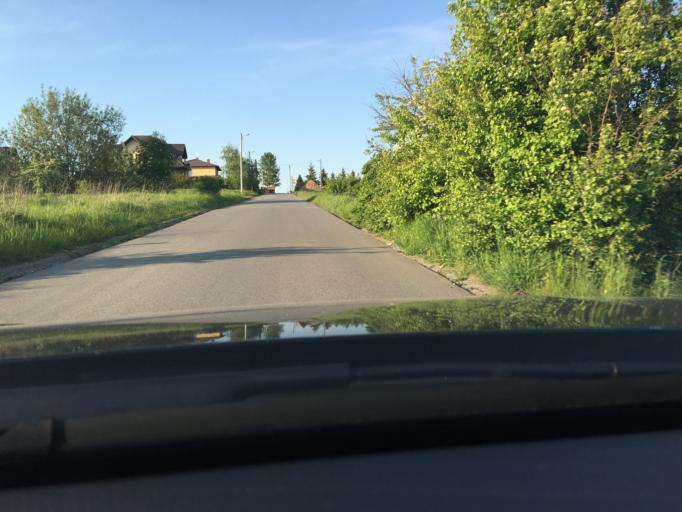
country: PL
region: Lesser Poland Voivodeship
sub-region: Powiat krakowski
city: Jerzmanowice
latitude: 50.2194
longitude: 19.7468
